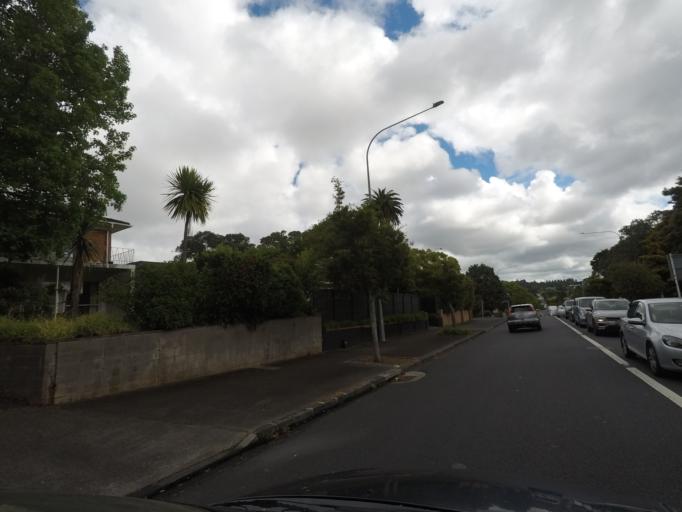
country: NZ
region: Auckland
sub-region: Auckland
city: Auckland
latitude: -36.8829
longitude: 174.8074
